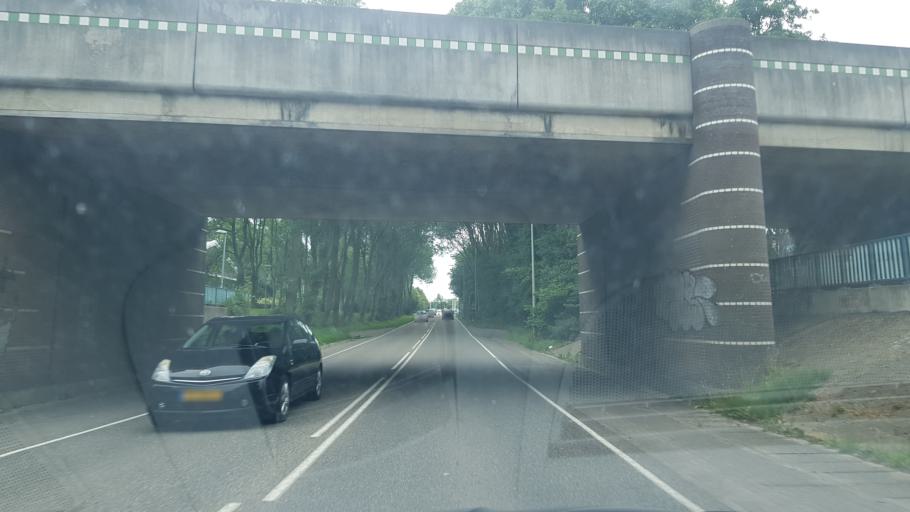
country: NL
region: North Holland
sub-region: Gemeente Hoorn
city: Hoorn
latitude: 52.6486
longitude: 5.0781
